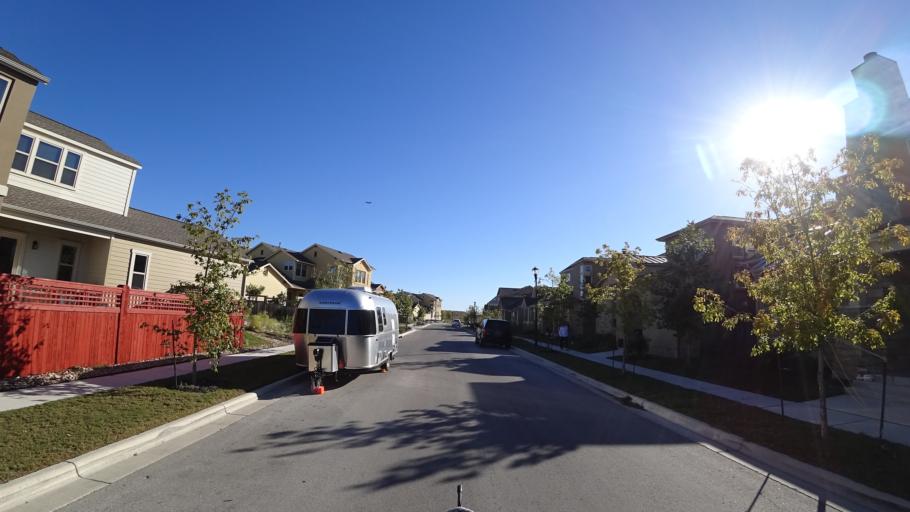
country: US
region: Texas
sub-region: Travis County
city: Austin
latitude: 30.2913
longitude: -97.6964
